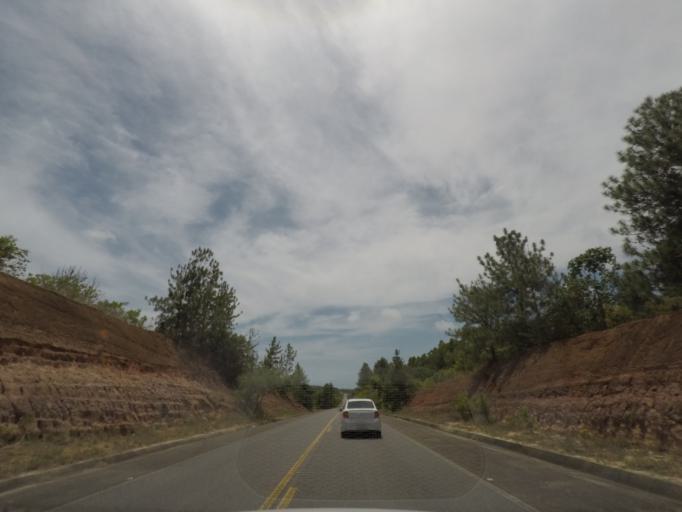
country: BR
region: Bahia
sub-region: Conde
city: Conde
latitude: -12.0086
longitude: -37.6865
